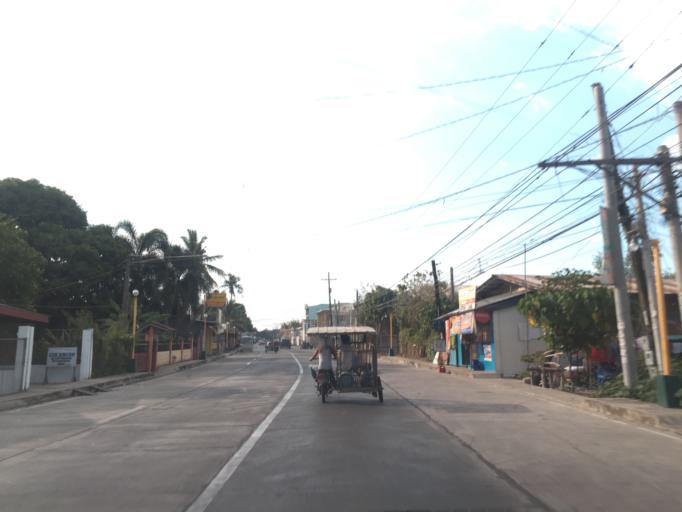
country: PH
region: Ilocos
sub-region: Province of Pangasinan
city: Bolingit
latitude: 15.9352
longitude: 120.3472
